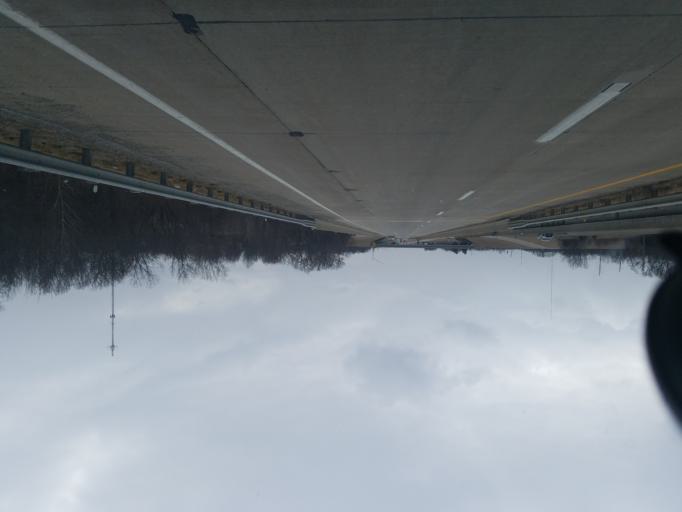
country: US
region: Missouri
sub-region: Randolph County
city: Moberly
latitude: 39.4213
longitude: -92.4119
